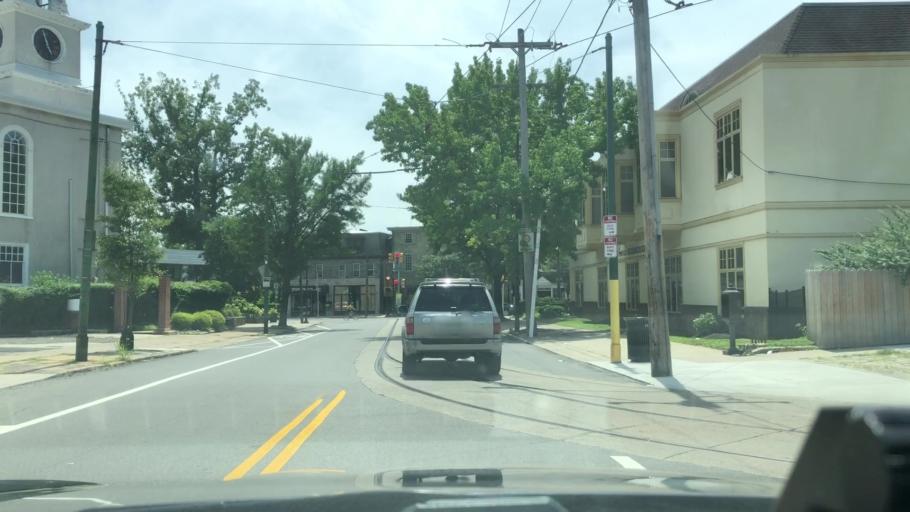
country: US
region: Pennsylvania
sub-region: Montgomery County
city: Wyndmoor
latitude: 40.0778
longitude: -75.2081
